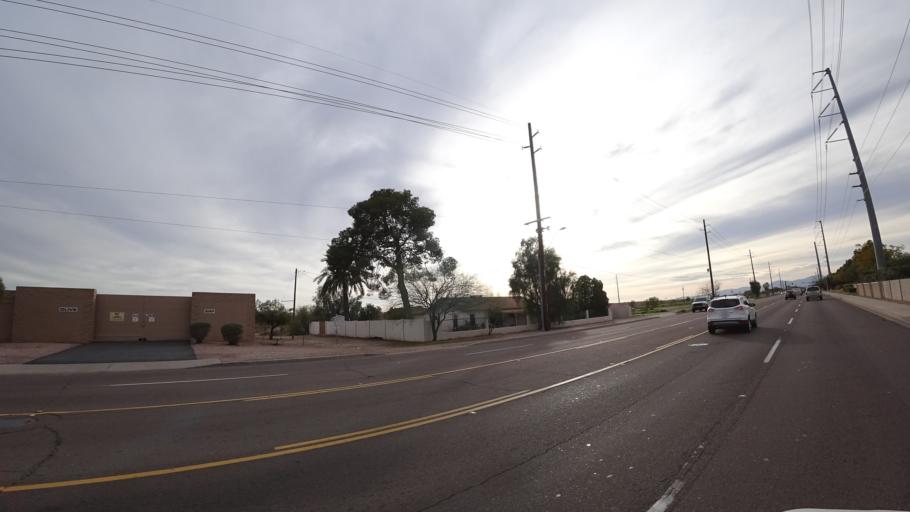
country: US
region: Arizona
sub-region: Maricopa County
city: Peoria
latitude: 33.5672
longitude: -112.2081
